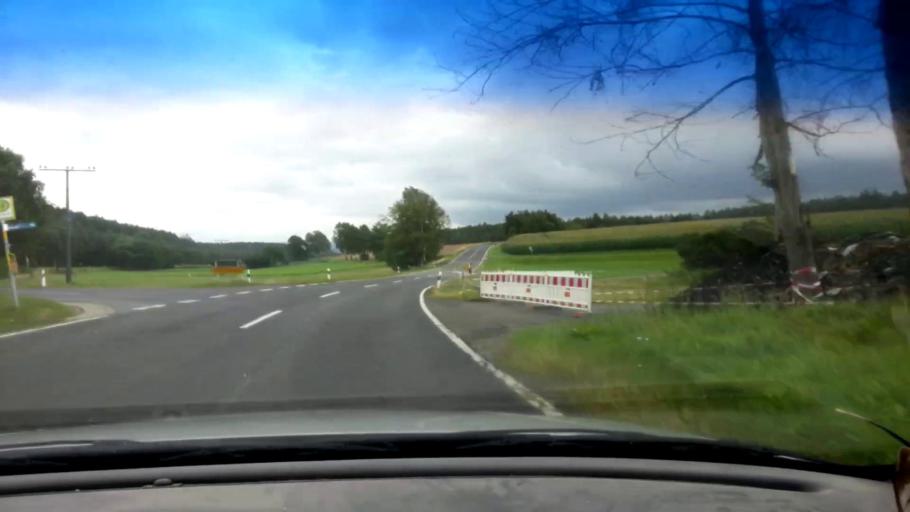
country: DE
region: Bavaria
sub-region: Upper Palatinate
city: Waldsassen
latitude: 50.0330
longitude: 12.3014
